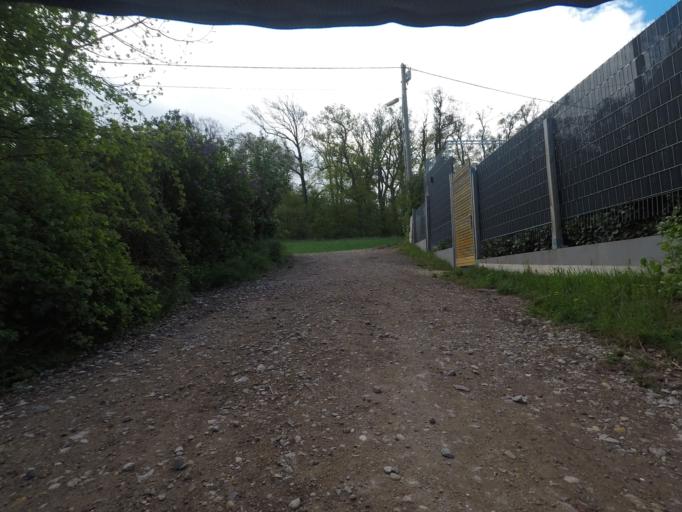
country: AT
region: Lower Austria
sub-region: Politischer Bezirk Modling
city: Perchtoldsdorf
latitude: 48.1739
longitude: 16.2633
